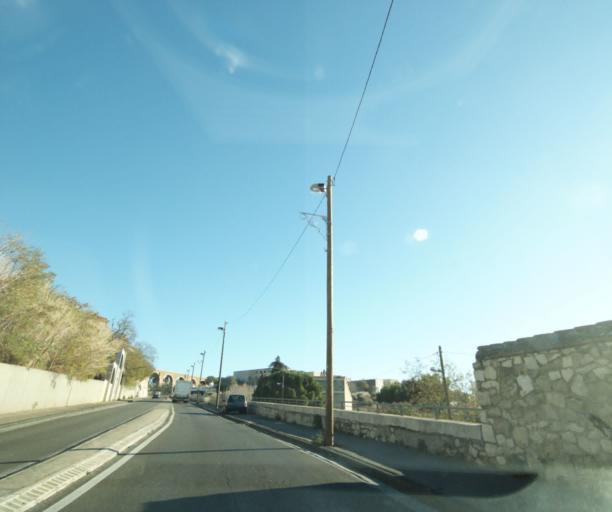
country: FR
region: Provence-Alpes-Cote d'Azur
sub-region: Departement des Bouches-du-Rhone
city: Marseille 16
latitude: 43.3494
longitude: 5.3542
